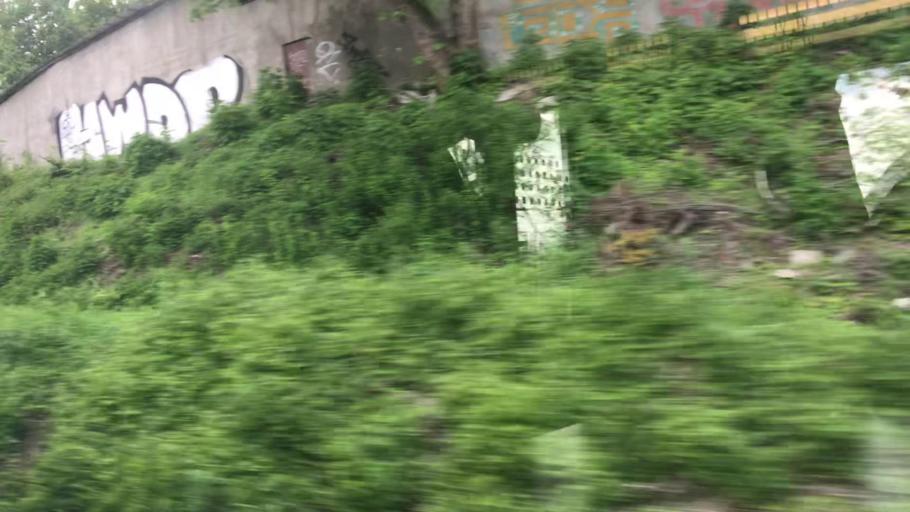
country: PL
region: Lower Silesian Voivodeship
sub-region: Powiat walbrzyski
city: Walbrzych
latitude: 50.7736
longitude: 16.2697
